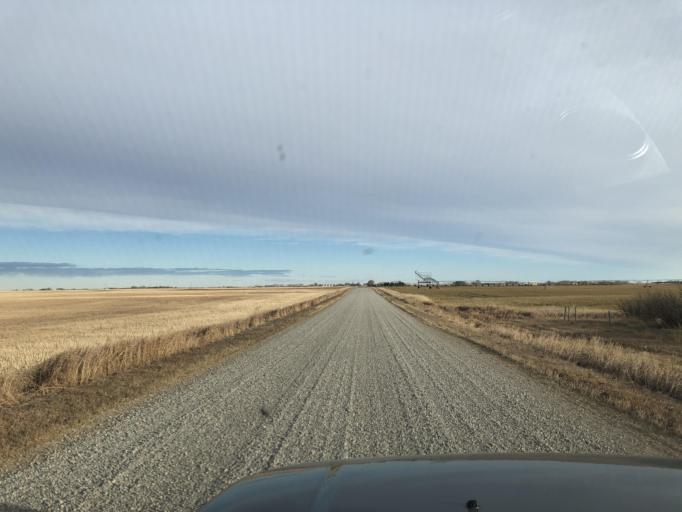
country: CA
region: Alberta
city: Strathmore
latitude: 50.8926
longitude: -113.5474
